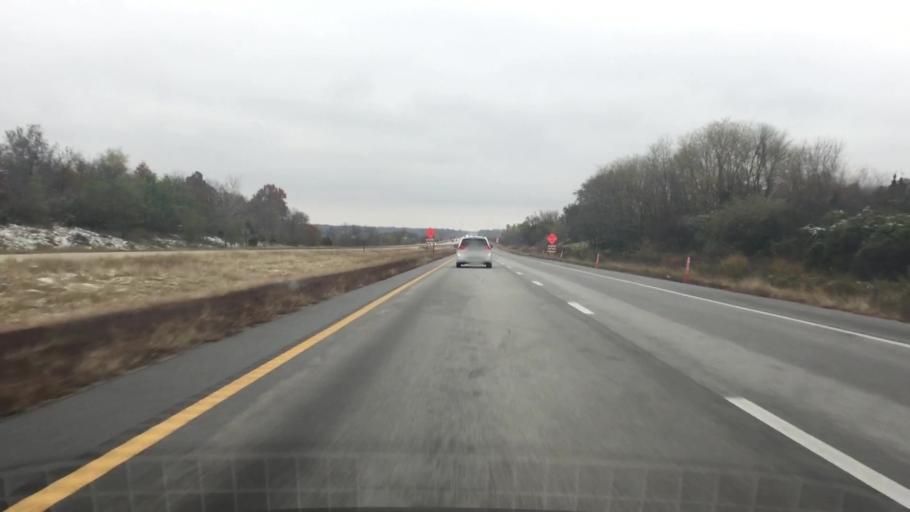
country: US
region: Missouri
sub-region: Henry County
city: Clinton
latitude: 38.2962
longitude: -93.7591
